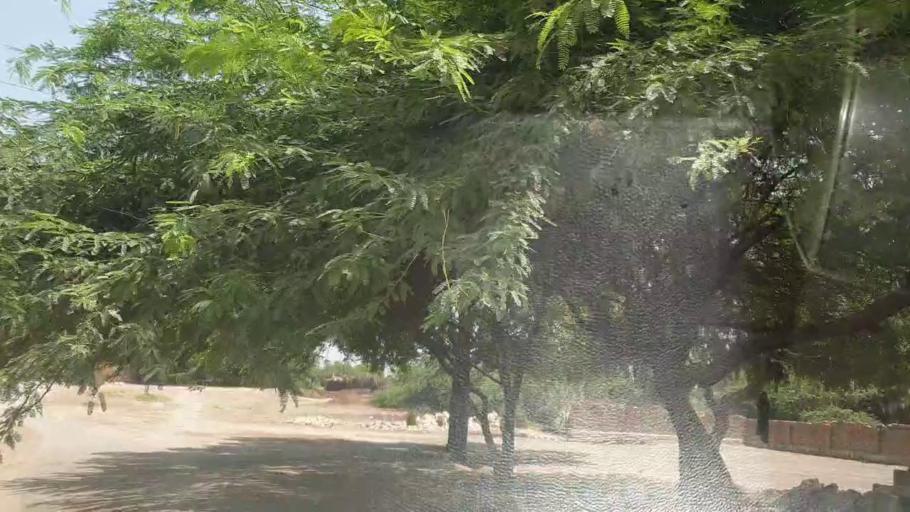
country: PK
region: Sindh
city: Kot Diji
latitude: 27.2853
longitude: 68.6413
